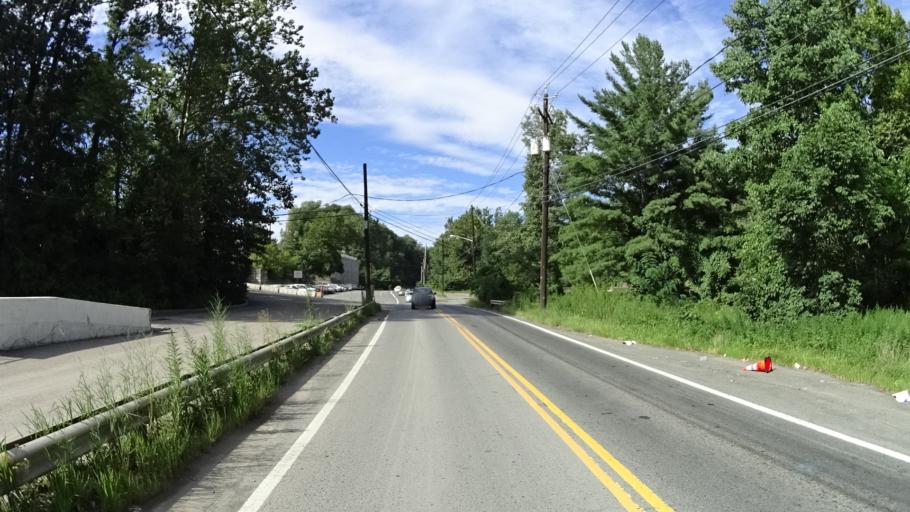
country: US
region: New Jersey
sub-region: Union County
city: Scotch Plains
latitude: 40.6576
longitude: -74.4037
